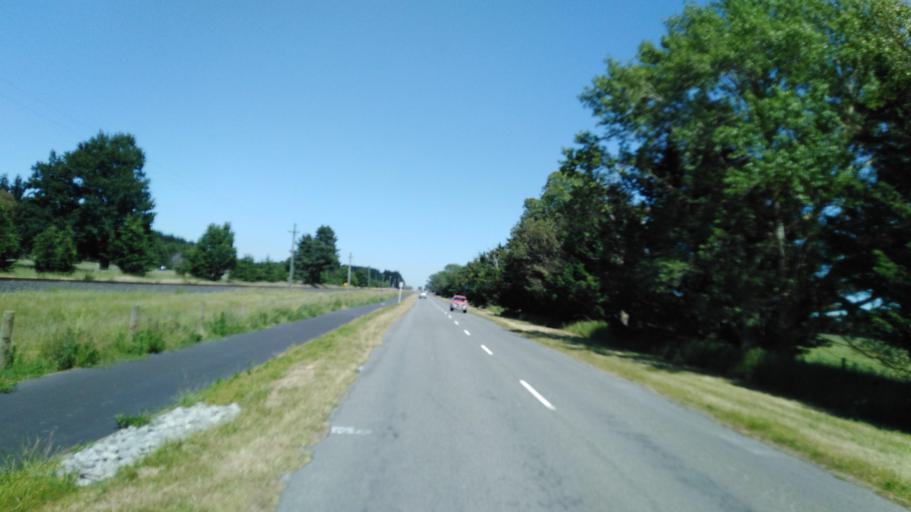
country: NZ
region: Canterbury
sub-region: Selwyn District
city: Prebbleton
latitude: -43.5580
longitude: 172.4638
